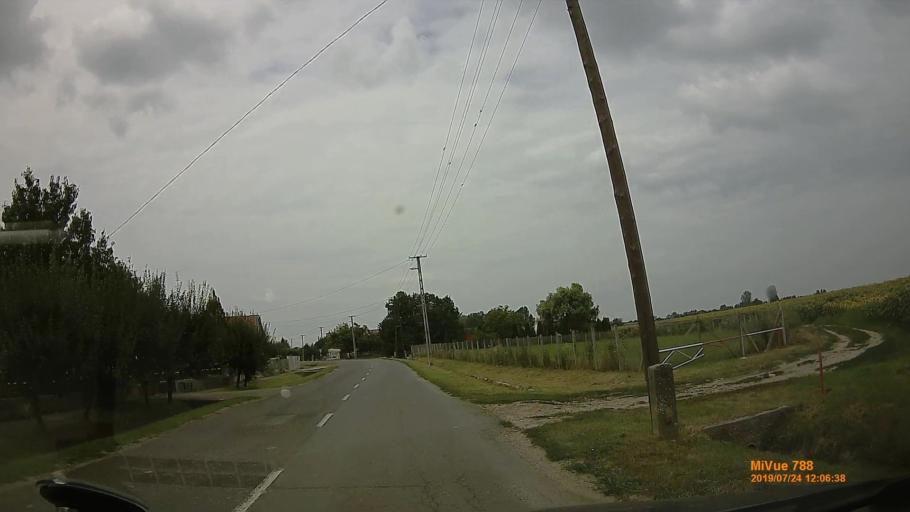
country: HU
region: Szabolcs-Szatmar-Bereg
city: Vasarosnameny
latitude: 48.1920
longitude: 22.4018
